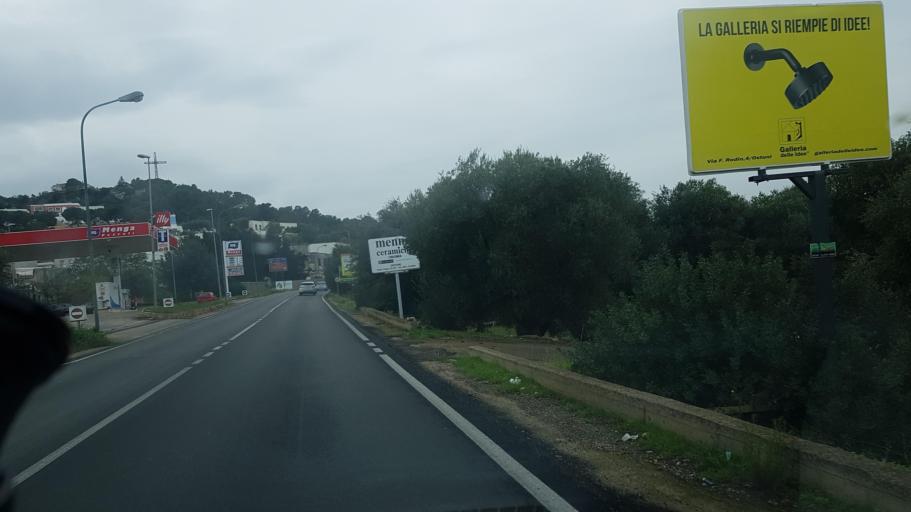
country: IT
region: Apulia
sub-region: Provincia di Brindisi
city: Ostuni
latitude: 40.7340
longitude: 17.5712
